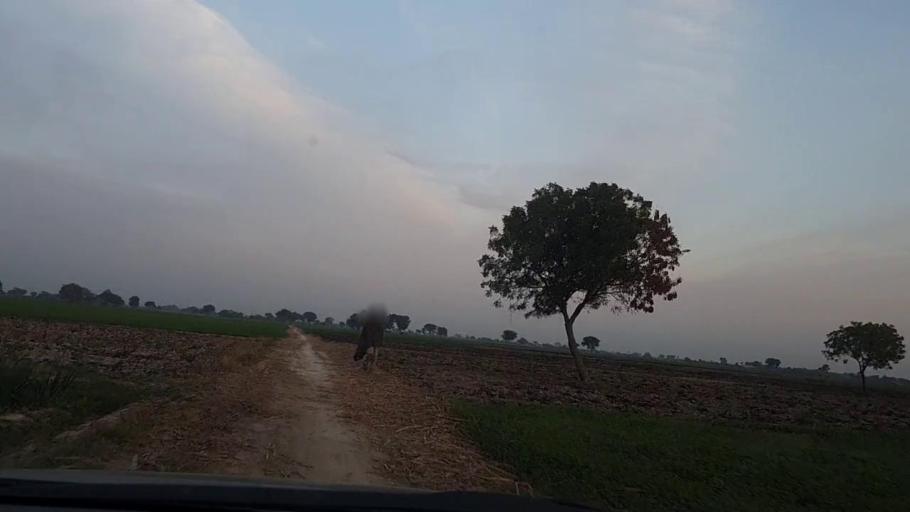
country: PK
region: Sindh
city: Sakrand
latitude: 26.1978
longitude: 68.3206
